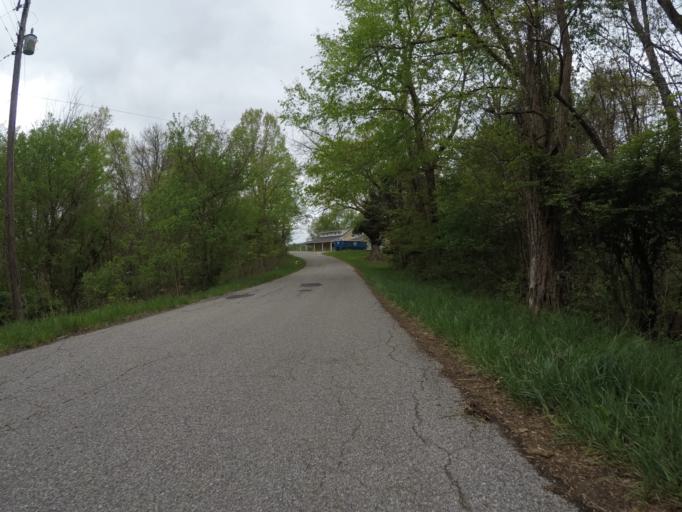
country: US
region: West Virginia
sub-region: Cabell County
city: Barboursville
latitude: 38.3958
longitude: -82.2519
